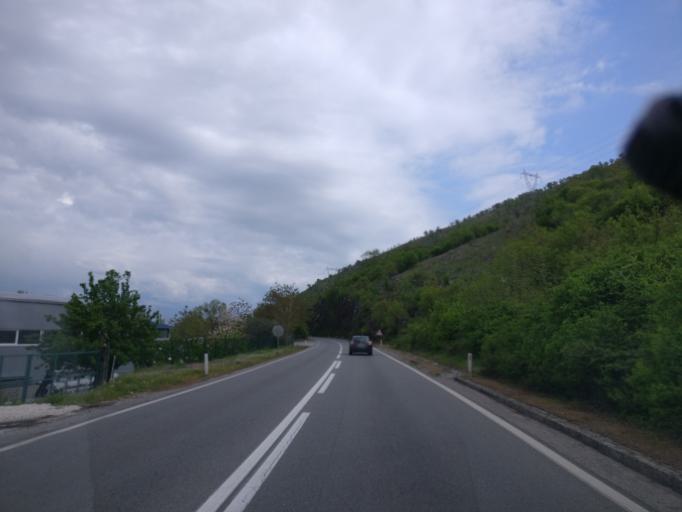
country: ME
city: Spuz
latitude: 42.4577
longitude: 19.1808
